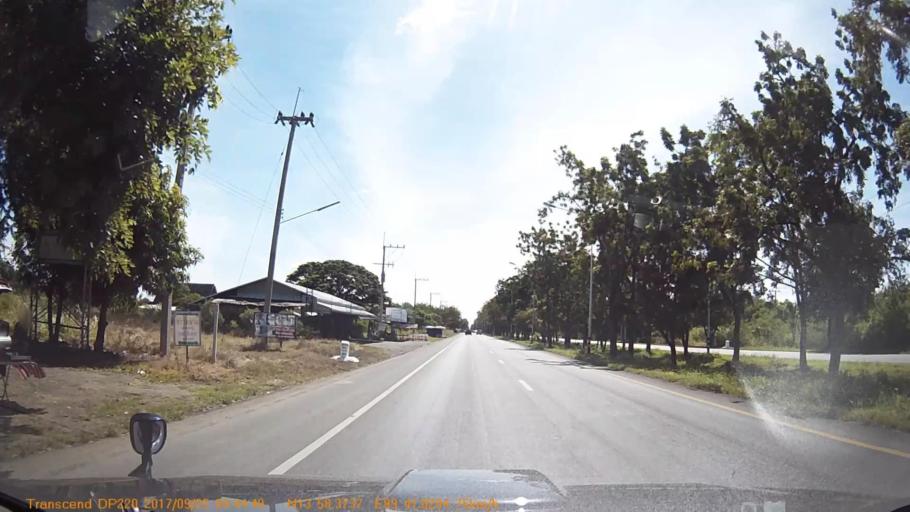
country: TH
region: Kanchanaburi
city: Tha Muang
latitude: 13.9728
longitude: 99.6841
